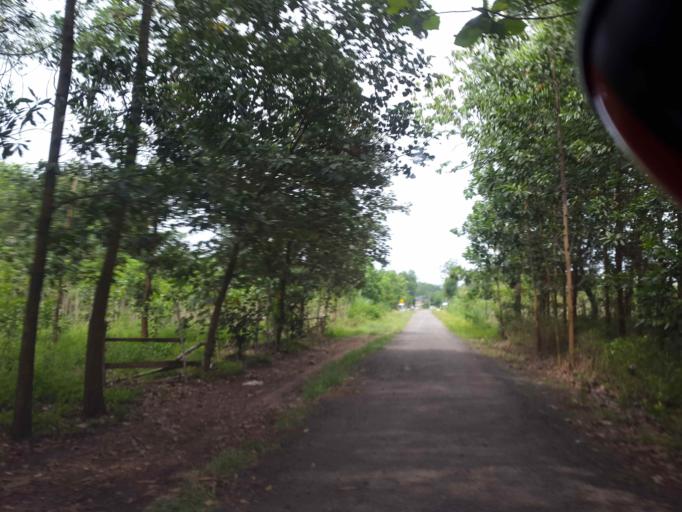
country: ID
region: Lampung
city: Natar
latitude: -5.2538
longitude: 105.2014
